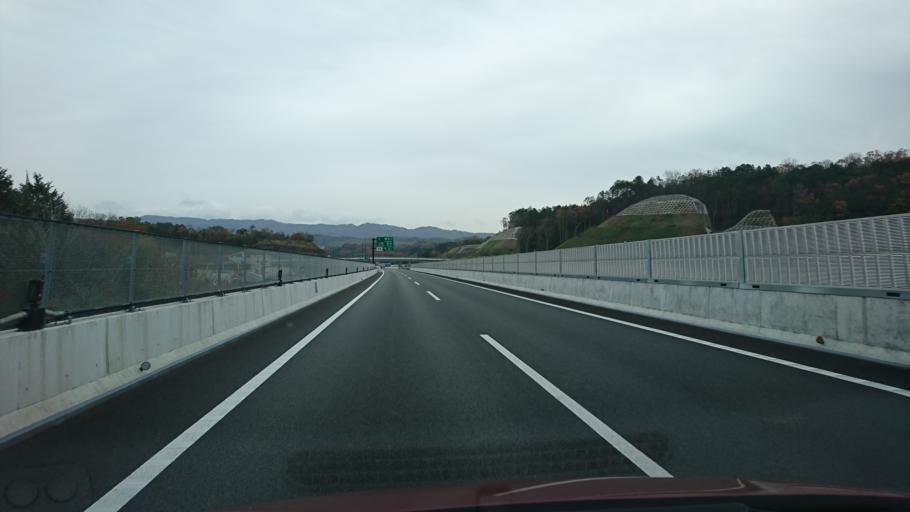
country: JP
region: Hyogo
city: Kawanishi
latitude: 34.8873
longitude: 135.3889
